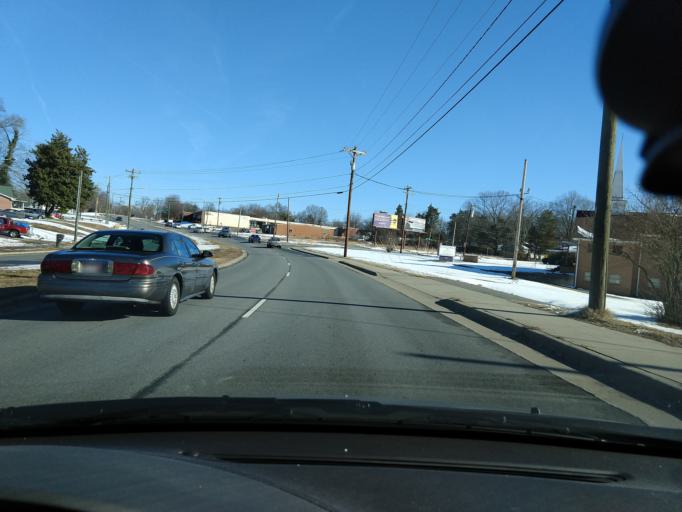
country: US
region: North Carolina
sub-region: Guilford County
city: Greensboro
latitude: 36.0457
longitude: -79.8119
